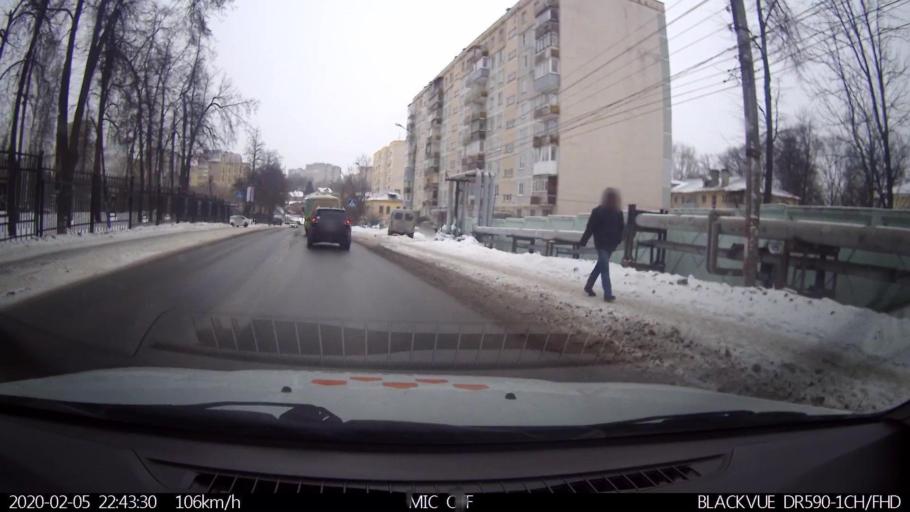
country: RU
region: Nizjnij Novgorod
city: Imeni Stepana Razina
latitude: 54.7120
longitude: 44.3790
